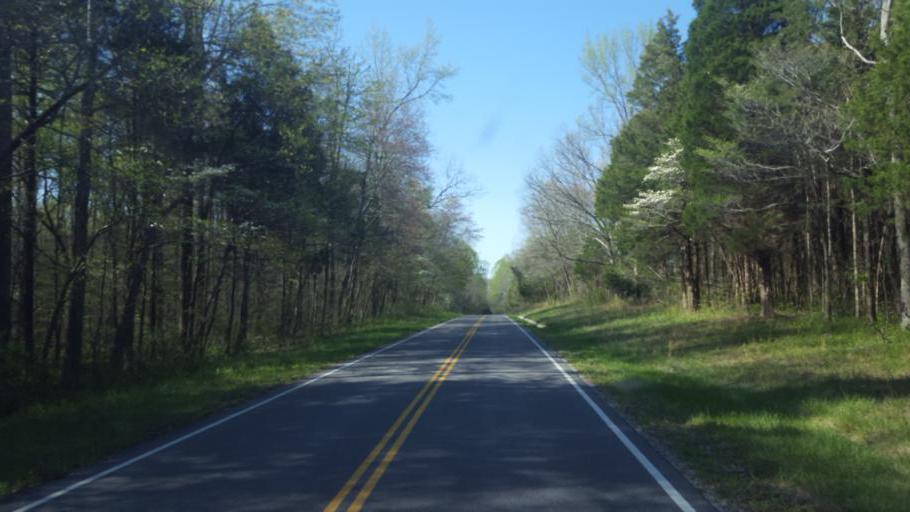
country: US
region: Kentucky
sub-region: Edmonson County
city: Brownsville
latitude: 37.1488
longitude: -86.1593
